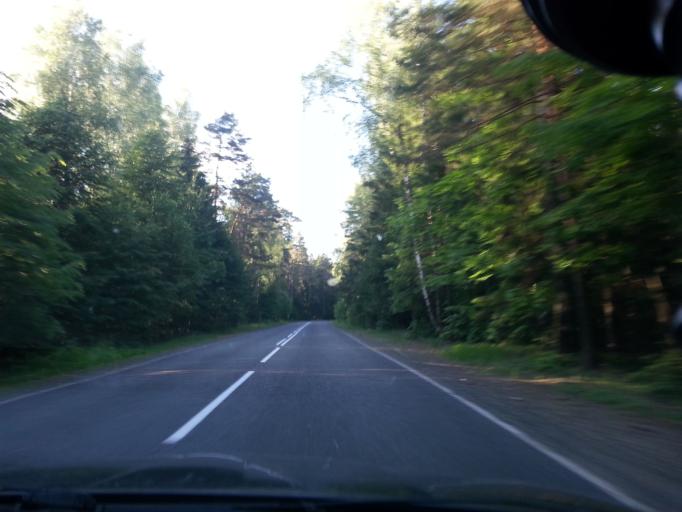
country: BY
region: Minsk
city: Narach
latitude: 54.9364
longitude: 26.5642
